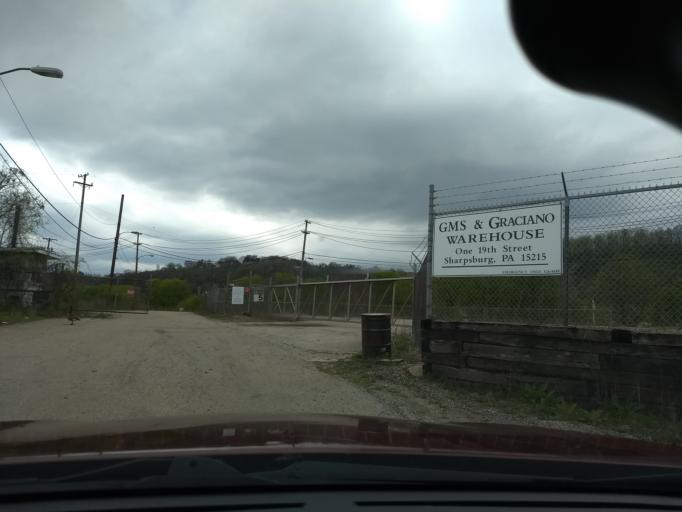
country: US
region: Pennsylvania
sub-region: Allegheny County
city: Sharpsburg
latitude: 40.4930
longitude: -79.9190
